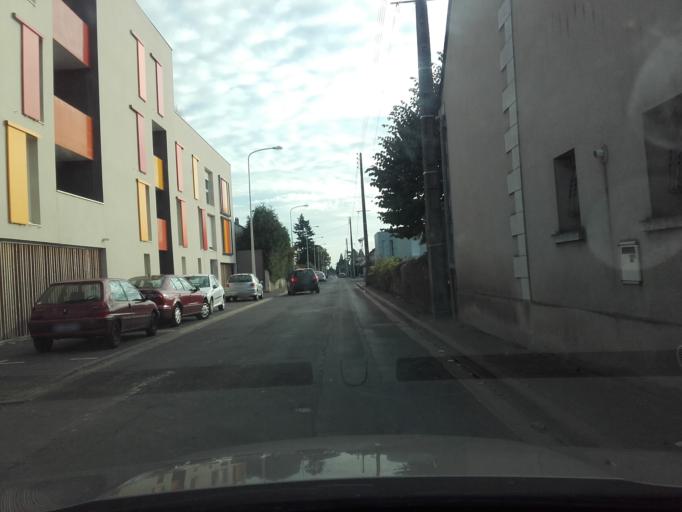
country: FR
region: Centre
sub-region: Departement d'Indre-et-Loire
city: Saint-Cyr-sur-Loire
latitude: 47.4185
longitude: 0.6973
